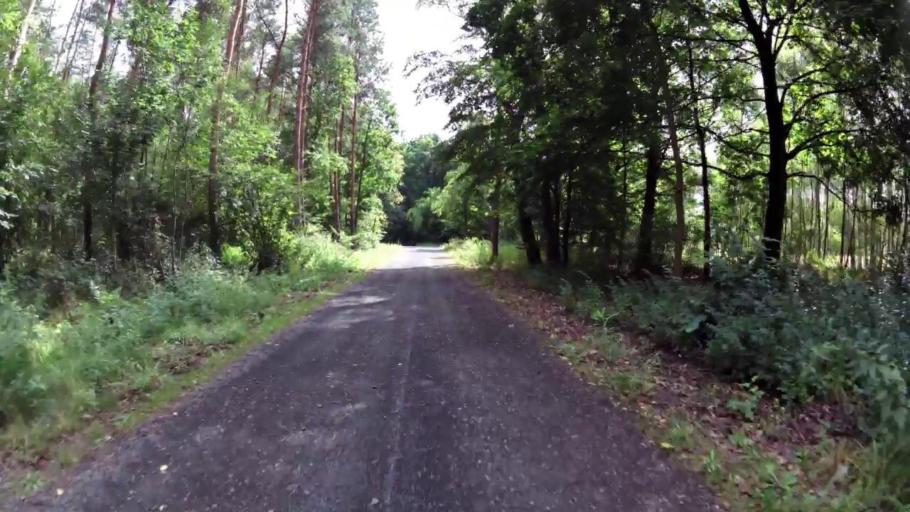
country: PL
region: West Pomeranian Voivodeship
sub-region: Powiat mysliborski
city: Debno
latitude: 52.7643
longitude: 14.7133
